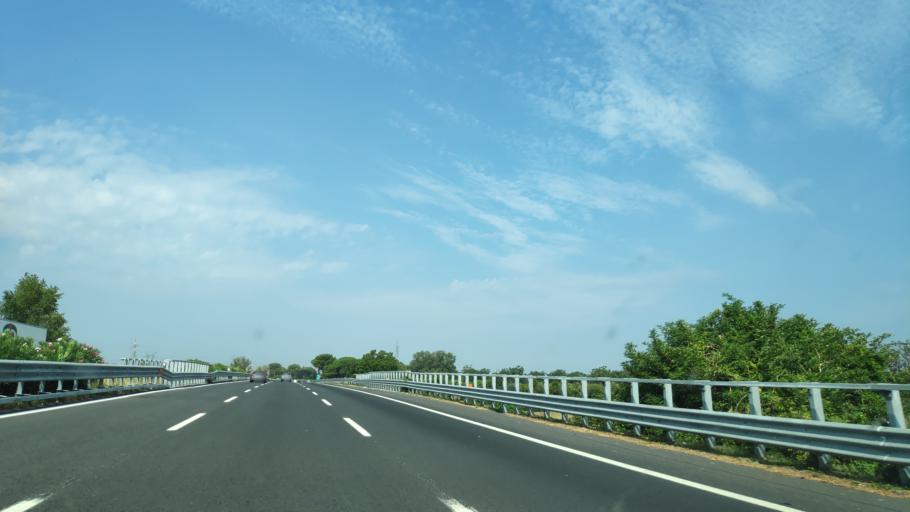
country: IT
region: Campania
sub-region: Provincia di Caserta
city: Maddaloni
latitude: 41.0112
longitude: 14.3891
